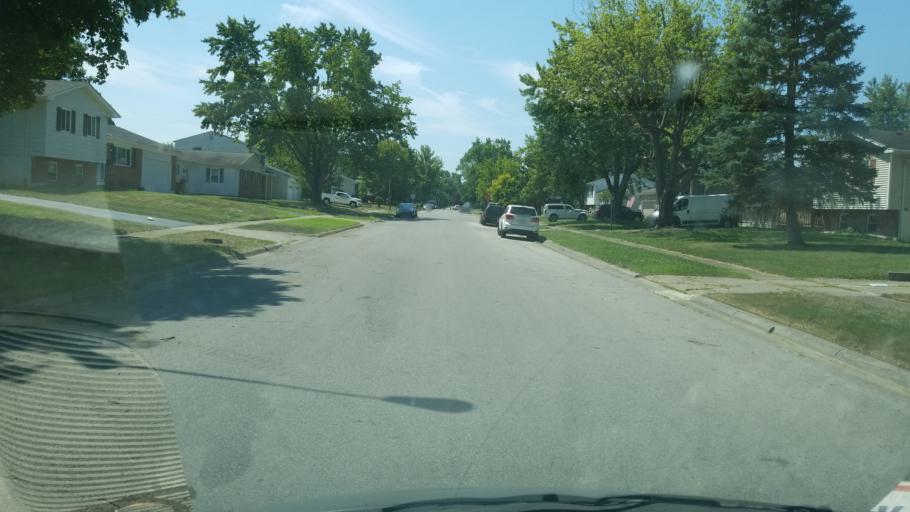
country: US
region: Ohio
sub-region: Franklin County
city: Grove City
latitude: 39.8947
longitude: -83.0729
